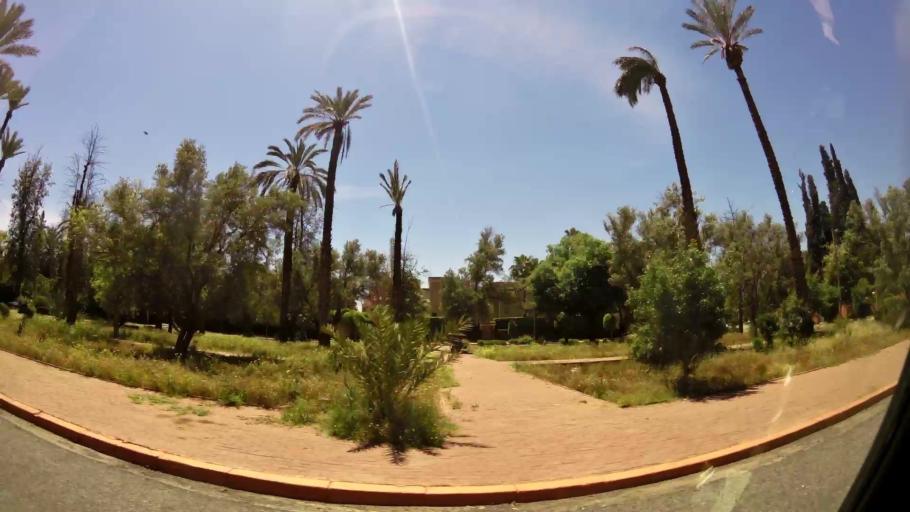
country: MA
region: Marrakech-Tensift-Al Haouz
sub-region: Marrakech
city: Marrakesh
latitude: 31.6244
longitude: -8.0103
